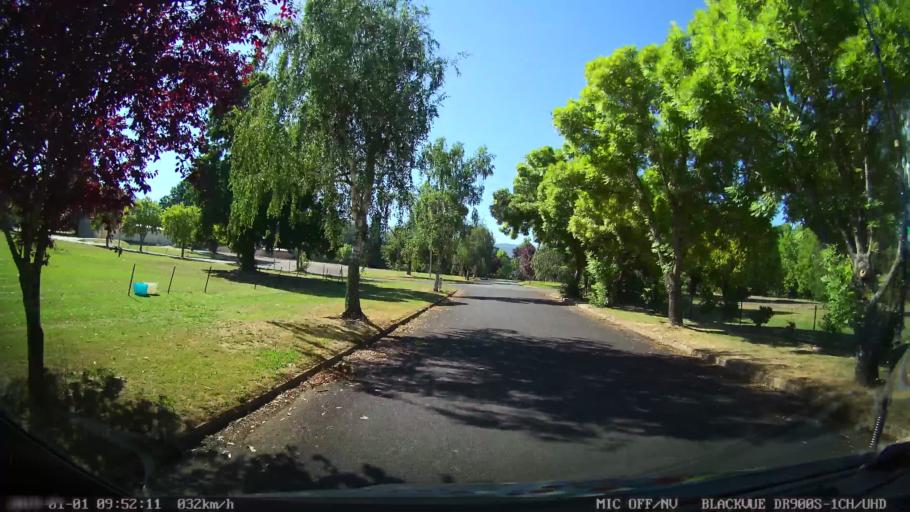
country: AU
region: New South Wales
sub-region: Snowy River
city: Jindabyne
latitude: -36.2170
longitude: 148.1237
